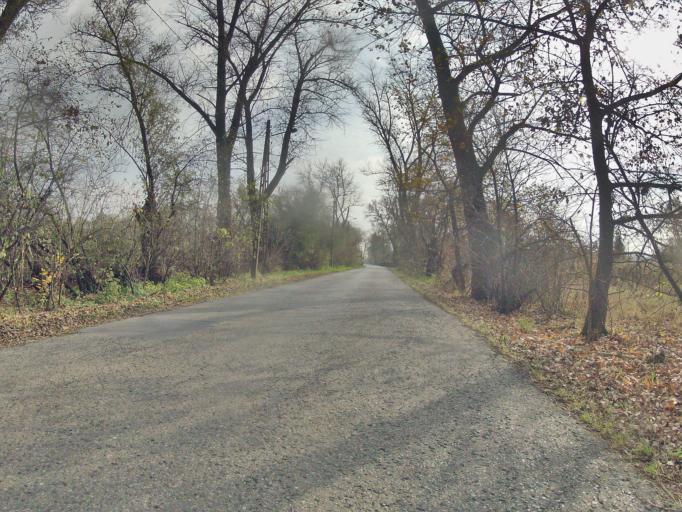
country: PL
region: Lesser Poland Voivodeship
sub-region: Powiat wielicki
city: Wegrzce Wielkie
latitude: 50.0614
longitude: 20.1075
